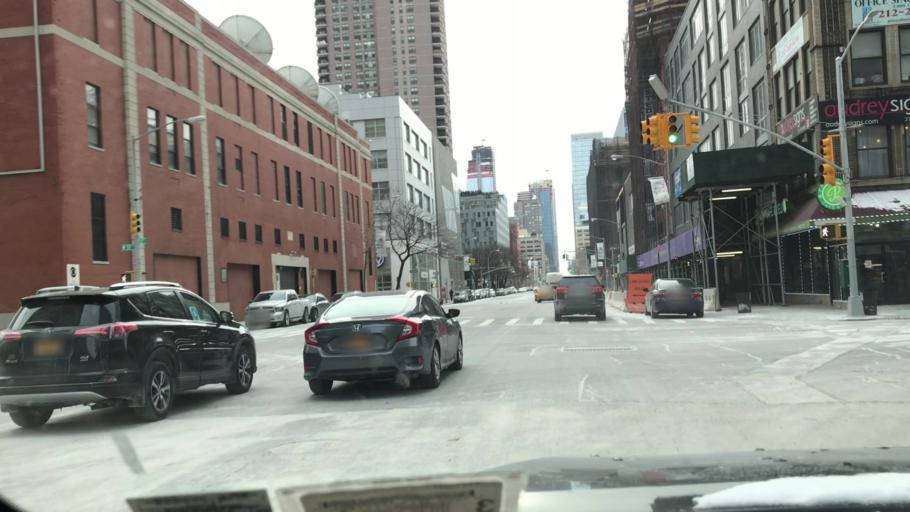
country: US
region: New Jersey
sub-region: Hudson County
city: Guttenberg
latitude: 40.7705
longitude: -73.9914
